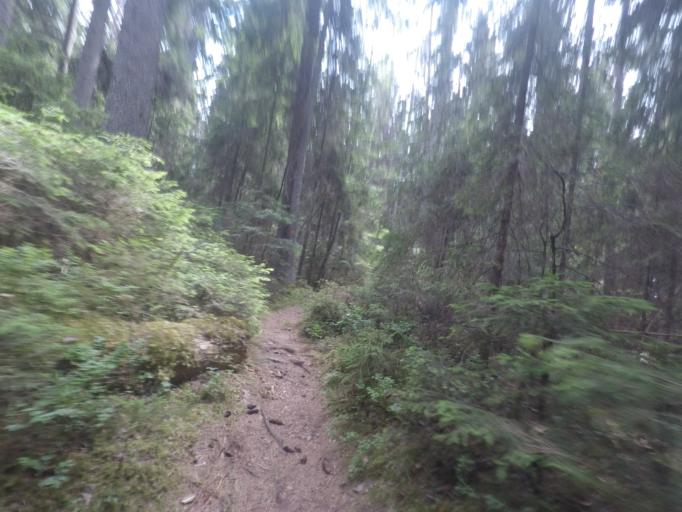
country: SE
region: Vaestmanland
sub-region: Kungsors Kommun
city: Kungsoer
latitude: 59.3628
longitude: 16.1047
